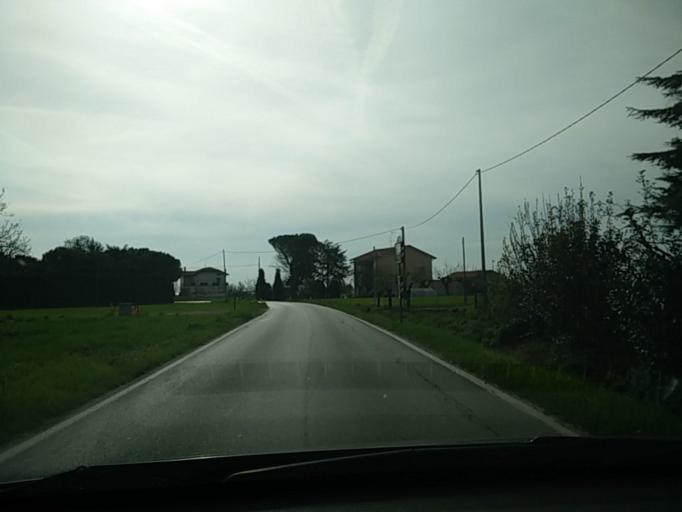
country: IT
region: Emilia-Romagna
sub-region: Provincia di Rimini
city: Santa Giustina
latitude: 44.0825
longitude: 12.4890
